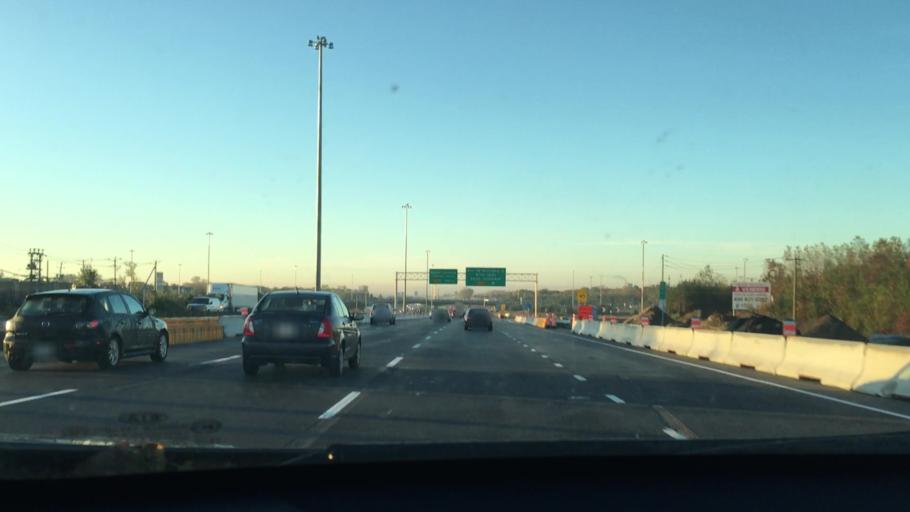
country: CA
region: Quebec
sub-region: Laurentides
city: Saint-Jerome
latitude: 45.7848
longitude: -74.0207
